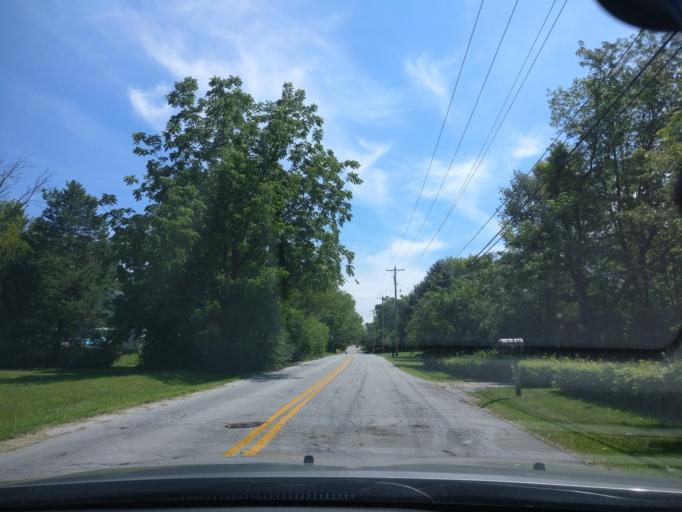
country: US
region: Ohio
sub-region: Montgomery County
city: Miamisburg
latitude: 39.6407
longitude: -84.2635
